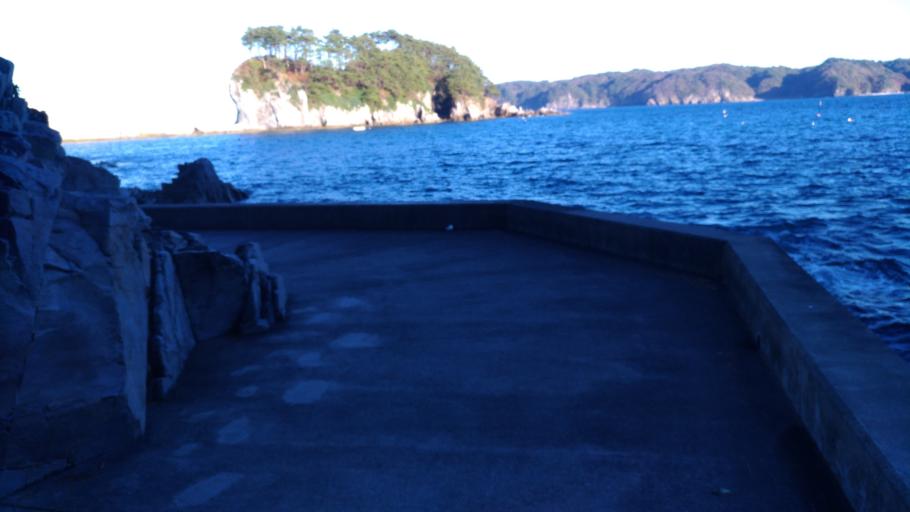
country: JP
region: Iwate
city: Miyako
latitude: 39.6502
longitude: 141.9801
